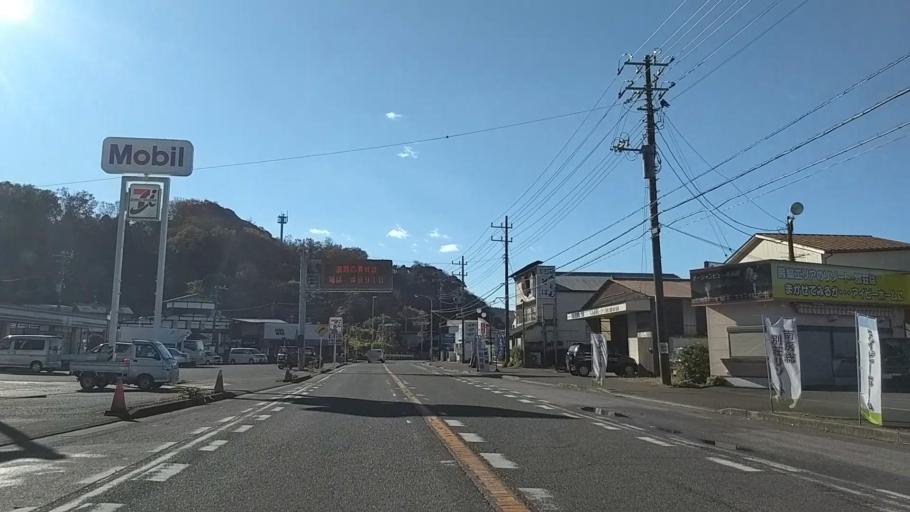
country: JP
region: Chiba
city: Futtsu
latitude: 35.2241
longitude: 139.8738
